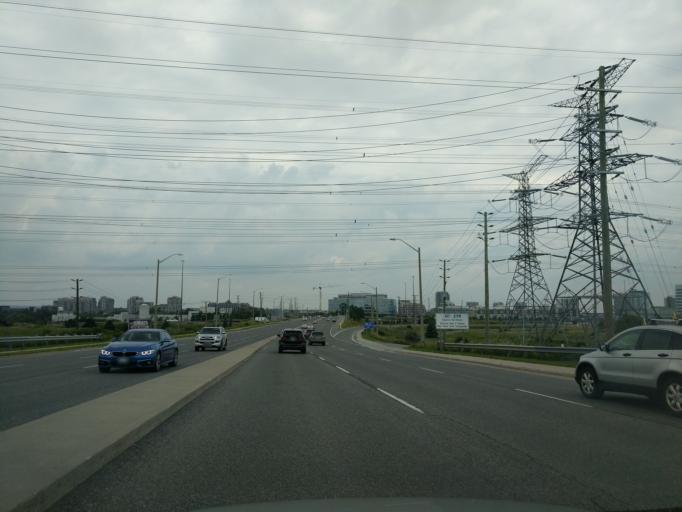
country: CA
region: Ontario
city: Markham
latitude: 43.8414
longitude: -79.3301
